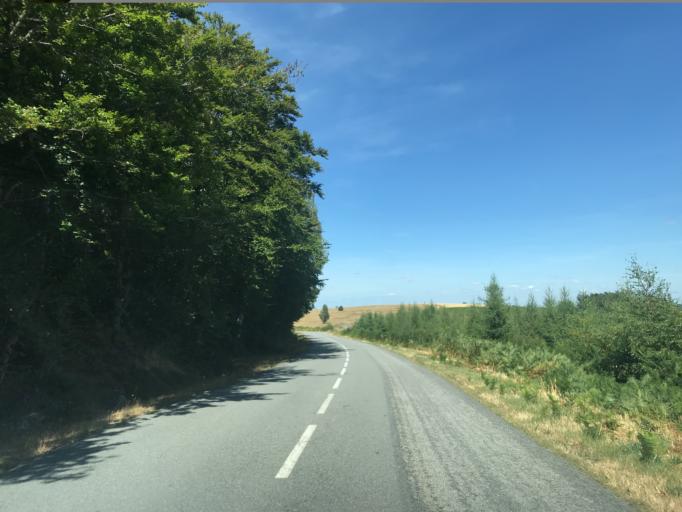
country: FR
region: Limousin
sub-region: Departement de la Creuse
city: La Courtine
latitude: 45.7480
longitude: 2.1434
